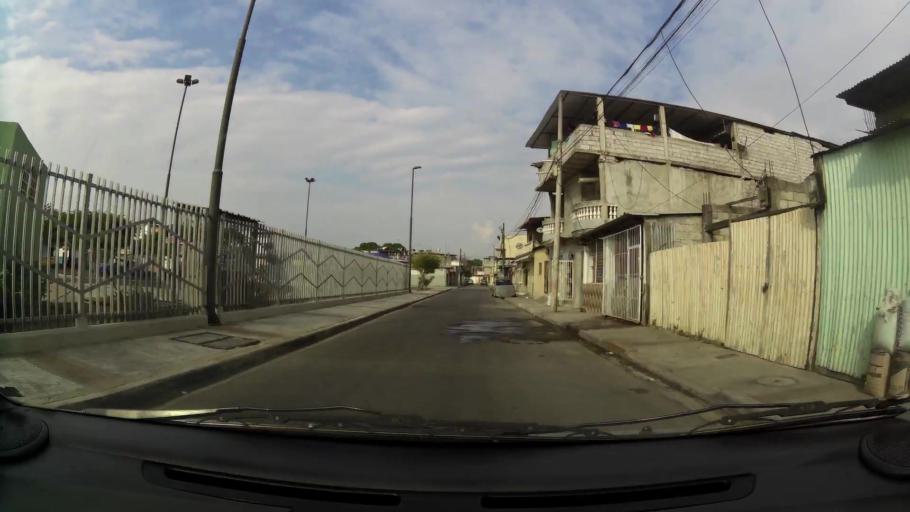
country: EC
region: Guayas
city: Guayaquil
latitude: -2.2461
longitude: -79.9076
